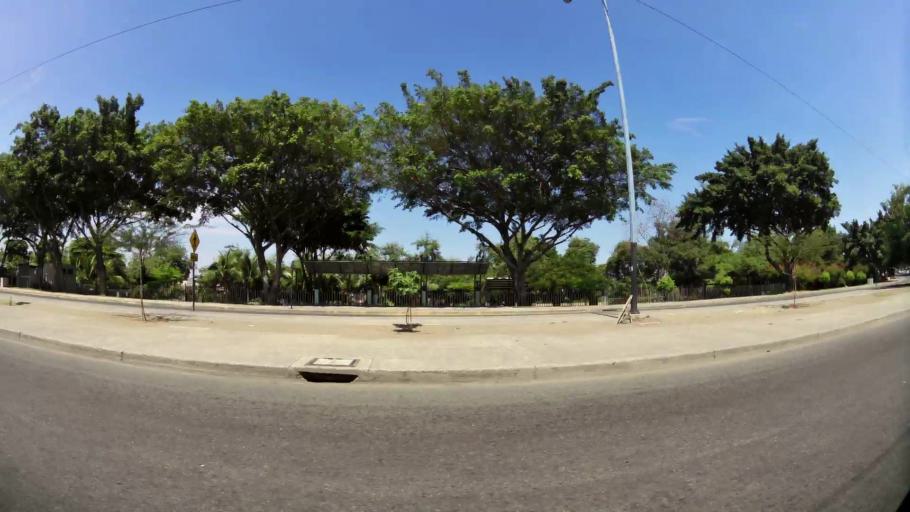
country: EC
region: Guayas
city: Guayaquil
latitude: -2.1881
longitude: -79.9278
